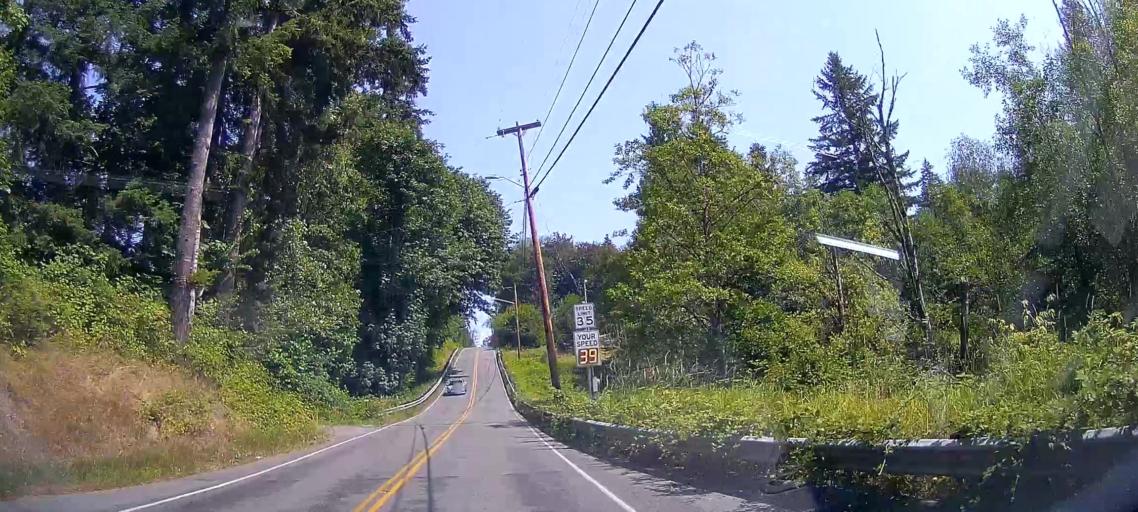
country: US
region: Washington
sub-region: Snohomish County
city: Sisco Heights
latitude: 48.0919
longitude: -122.1212
